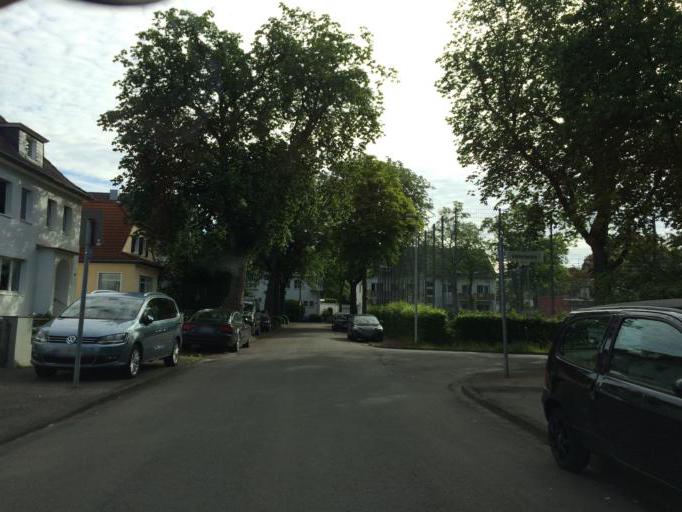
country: DE
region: North Rhine-Westphalia
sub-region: Regierungsbezirk Koln
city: Konigswinter
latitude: 50.6934
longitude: 7.1554
